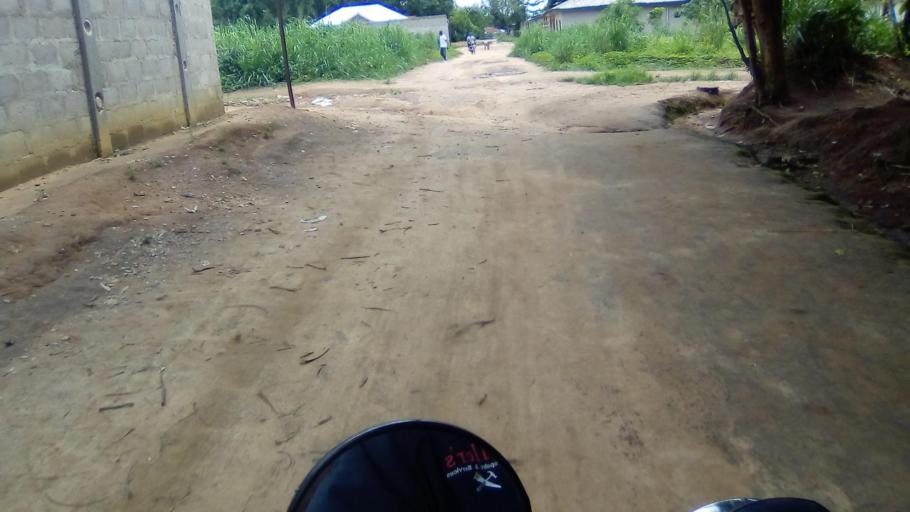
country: SL
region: Southern Province
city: Bo
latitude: 7.9368
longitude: -11.7221
